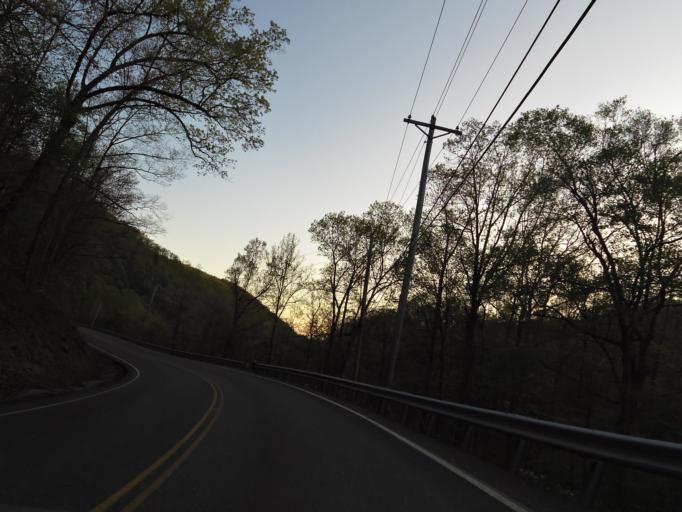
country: US
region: Tennessee
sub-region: Campbell County
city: LaFollette
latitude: 36.4157
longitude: -84.0961
